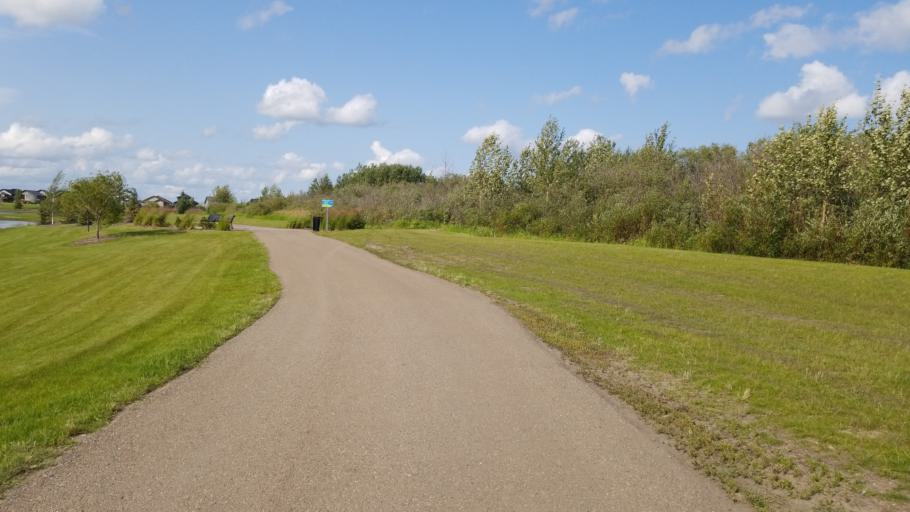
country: CA
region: Saskatchewan
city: Lloydminster
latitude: 53.2605
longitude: -110.0471
